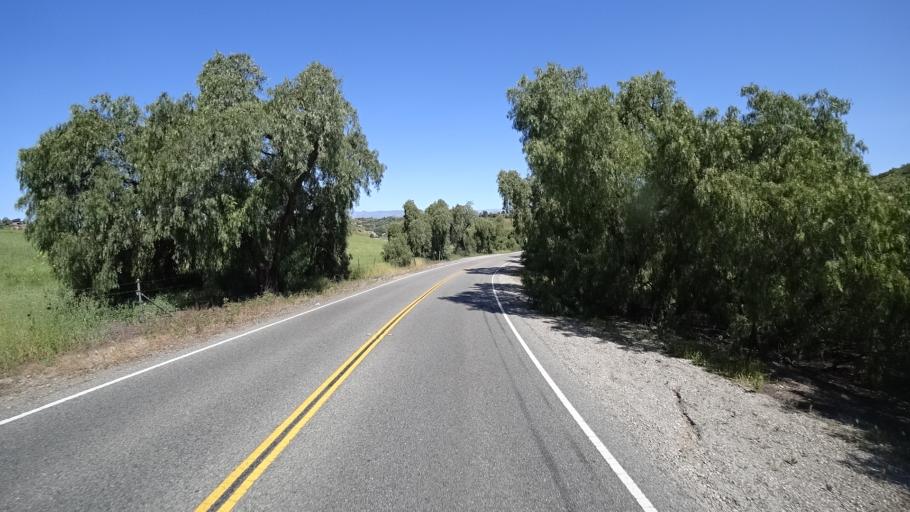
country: US
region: California
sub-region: Ventura County
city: Moorpark
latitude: 34.2398
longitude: -118.8628
